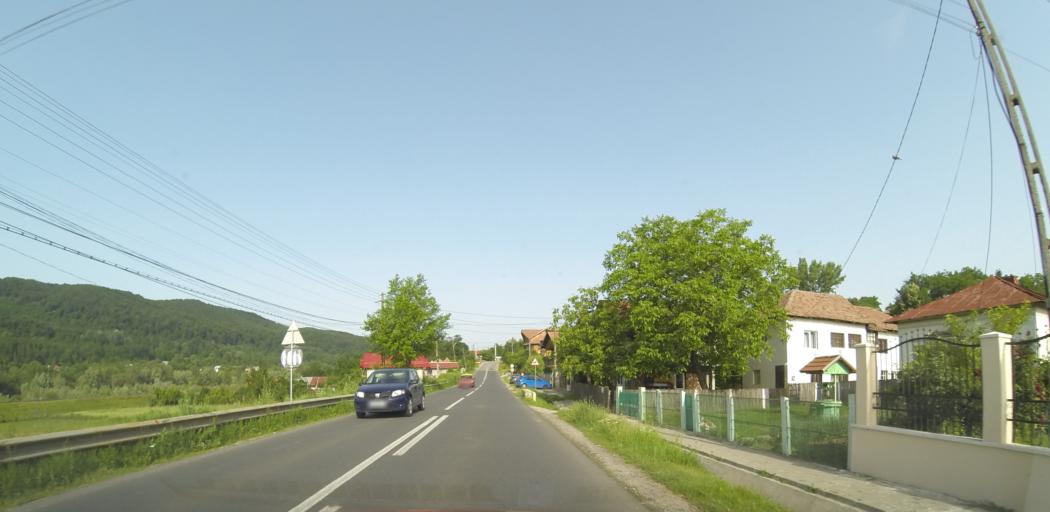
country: RO
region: Valcea
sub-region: Comuna Vladesti
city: Vladesti
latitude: 45.1218
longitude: 24.2945
